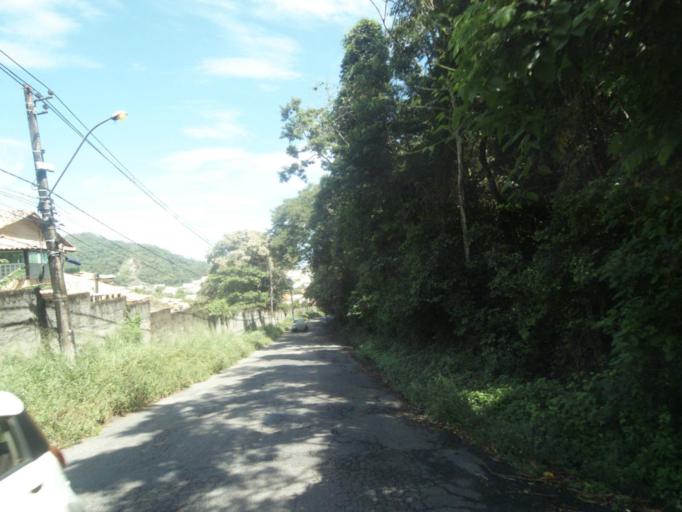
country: BR
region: Rio de Janeiro
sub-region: Niteroi
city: Niteroi
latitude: -22.9635
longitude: -43.0275
